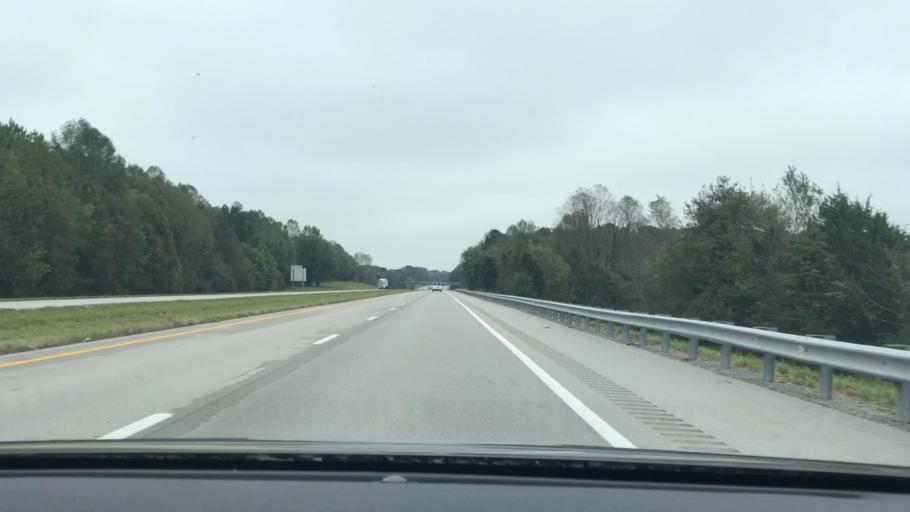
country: US
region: Kentucky
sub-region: Pulaski County
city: Somerset
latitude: 37.0960
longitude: -84.7819
